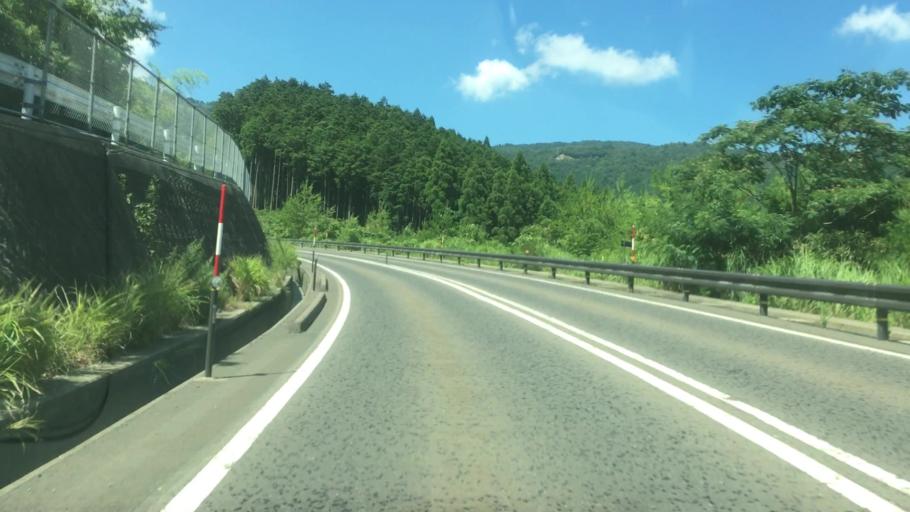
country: JP
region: Tottori
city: Tottori
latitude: 35.2818
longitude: 134.2266
